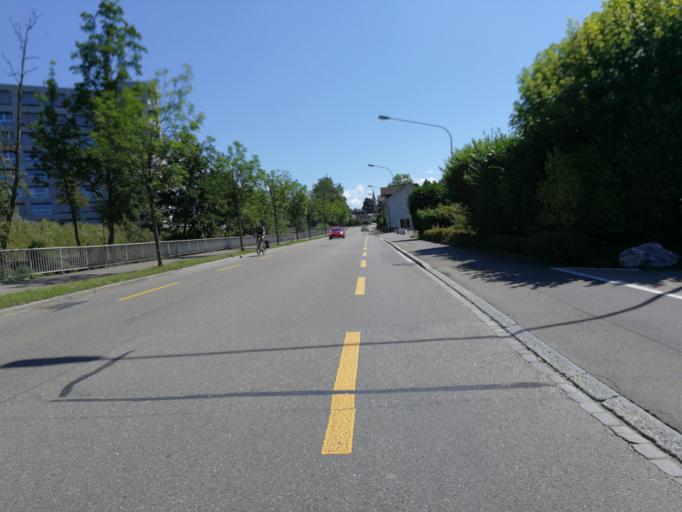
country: CH
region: Zurich
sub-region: Bezirk Uster
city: Uster / Nieder-Uster
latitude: 47.3450
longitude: 8.7044
